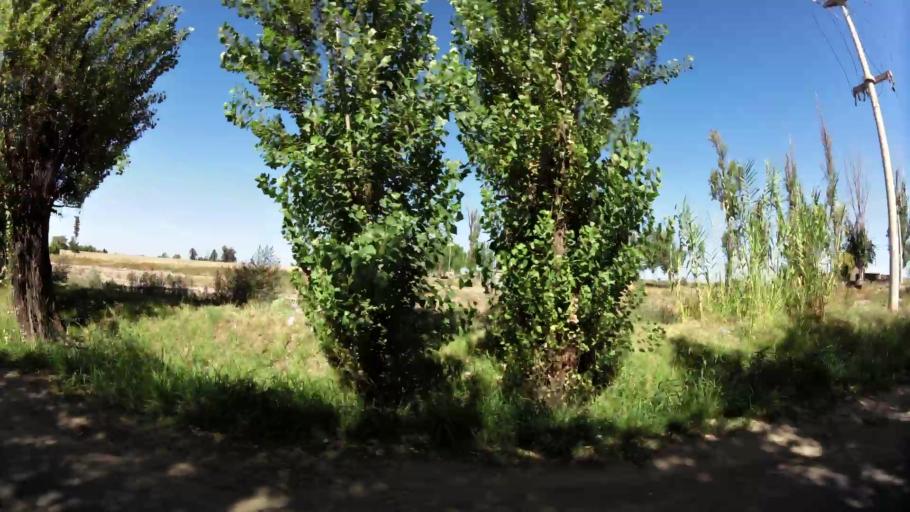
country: AR
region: Mendoza
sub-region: Departamento de Godoy Cruz
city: Godoy Cruz
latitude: -32.9532
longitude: -68.8226
